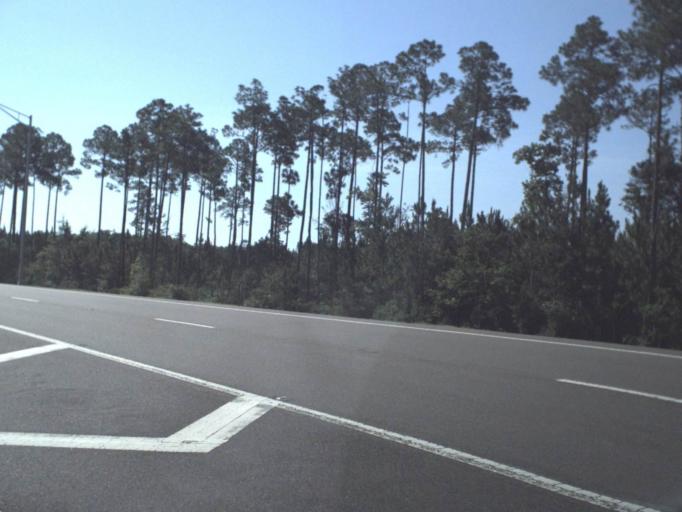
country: US
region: Florida
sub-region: Nassau County
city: Nassau Village-Ratliff
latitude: 30.4856
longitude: -81.6699
